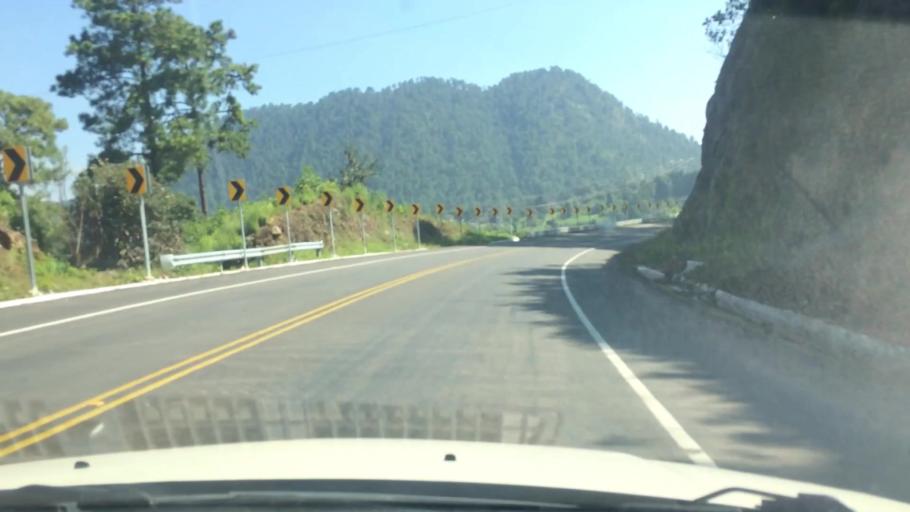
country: MX
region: Mexico
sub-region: Amanalco
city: Polvillos (San Bartolo Quinta Seccion)
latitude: 19.2275
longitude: -100.0829
